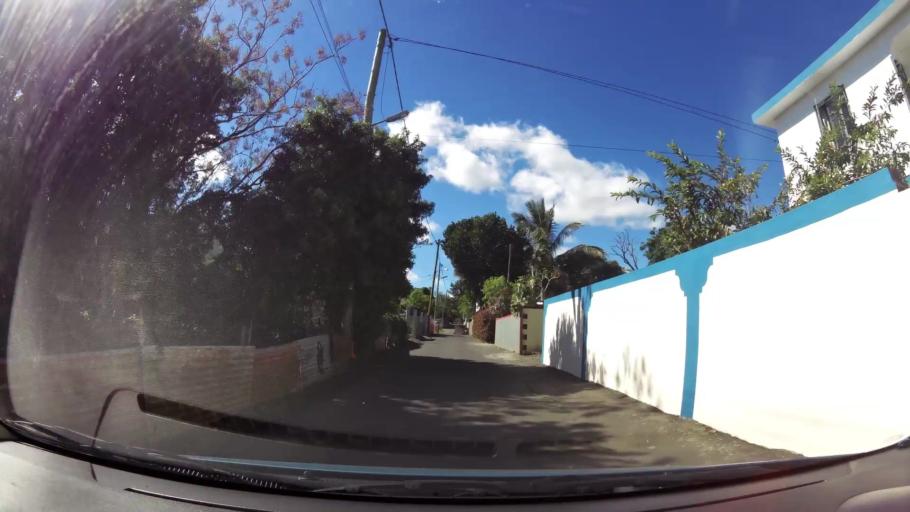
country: MU
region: Plaines Wilhems
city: Vacoas
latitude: -20.3097
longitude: 57.4731
